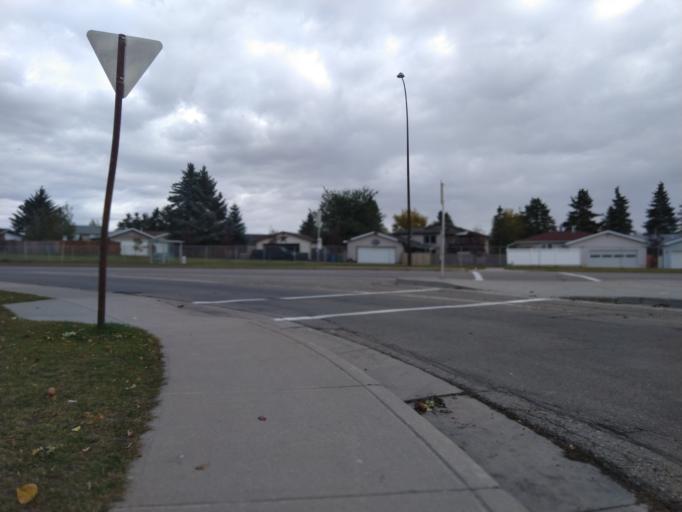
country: CA
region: Alberta
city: Calgary
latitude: 51.0210
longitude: -113.9996
